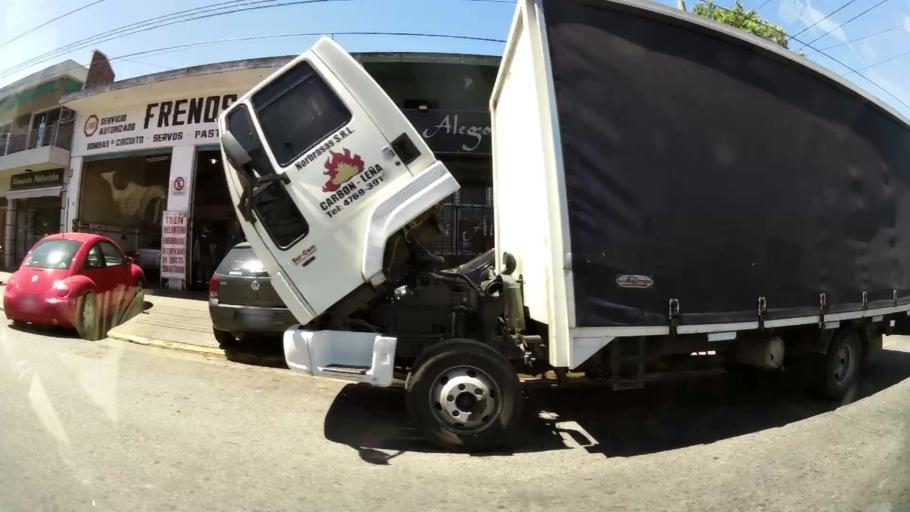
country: AR
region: Buenos Aires
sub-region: Partido de General San Martin
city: General San Martin
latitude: -34.5700
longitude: -58.5407
